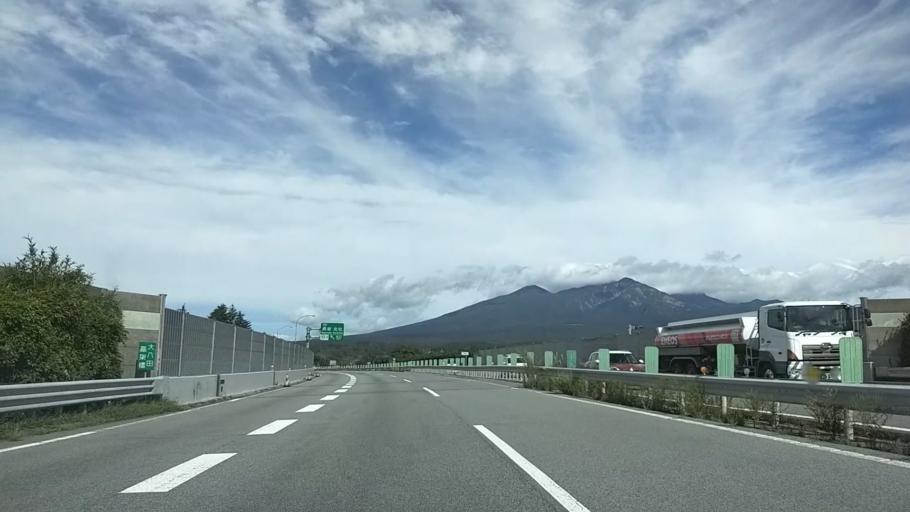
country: JP
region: Yamanashi
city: Nirasaki
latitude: 35.8332
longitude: 138.3917
